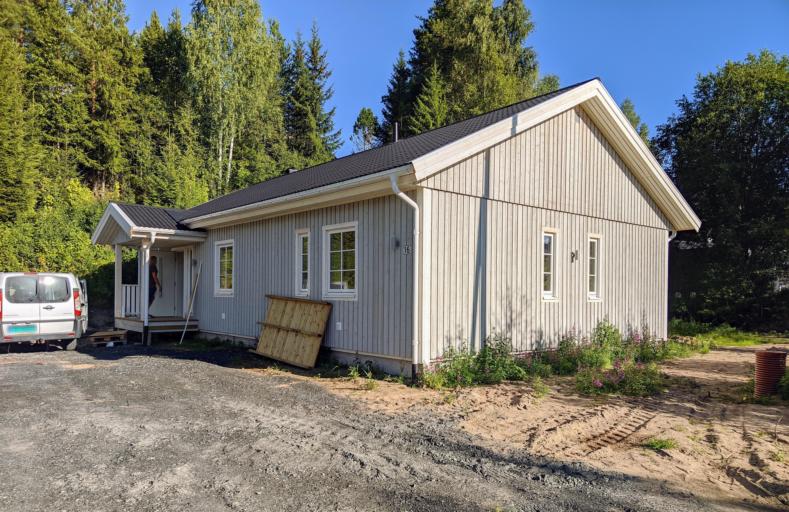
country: NO
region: Hedmark
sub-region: Elverum
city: Elverum
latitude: 60.8880
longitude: 11.5721
